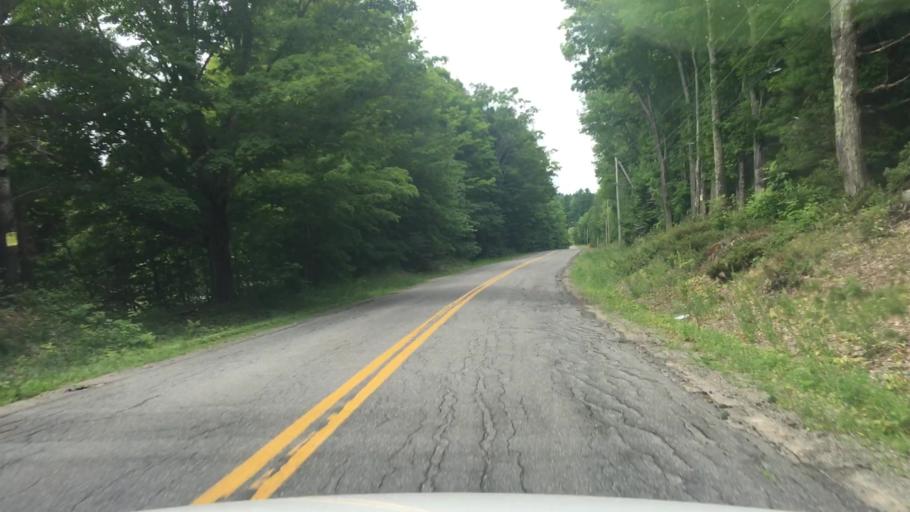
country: US
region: Maine
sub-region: Kennebec County
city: Albion
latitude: 44.5103
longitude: -69.3431
